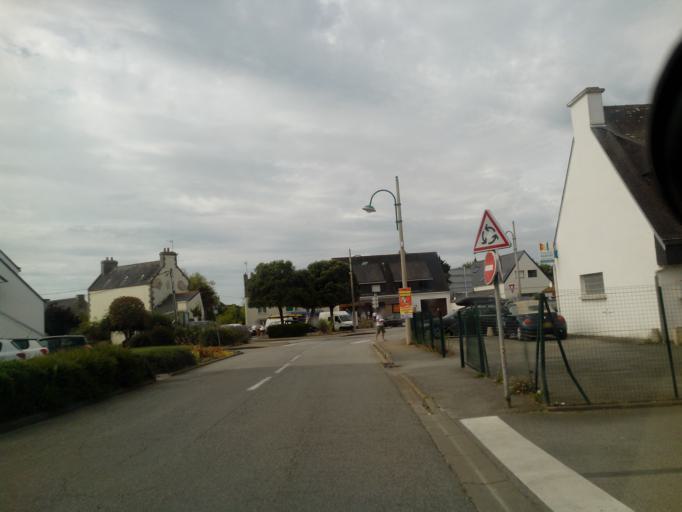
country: FR
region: Brittany
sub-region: Departement du Morbihan
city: Erdeven
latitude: 47.6400
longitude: -3.1534
